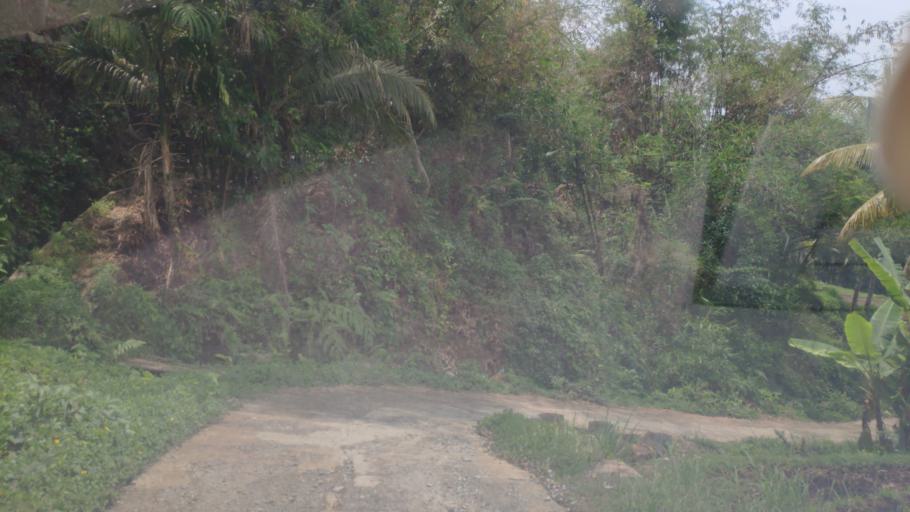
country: ID
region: Central Java
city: Gombong
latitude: -7.4299
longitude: 109.5600
